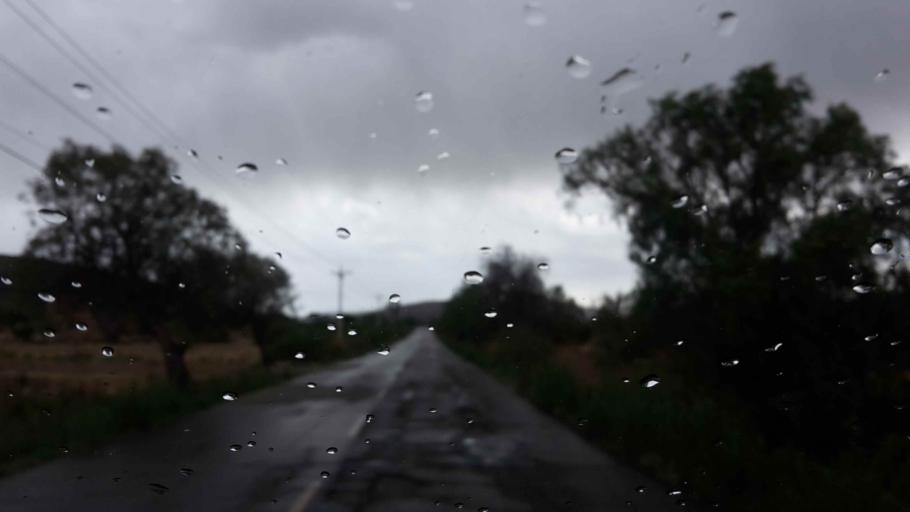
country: BO
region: Cochabamba
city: Tarata
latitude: -17.5699
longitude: -66.0714
